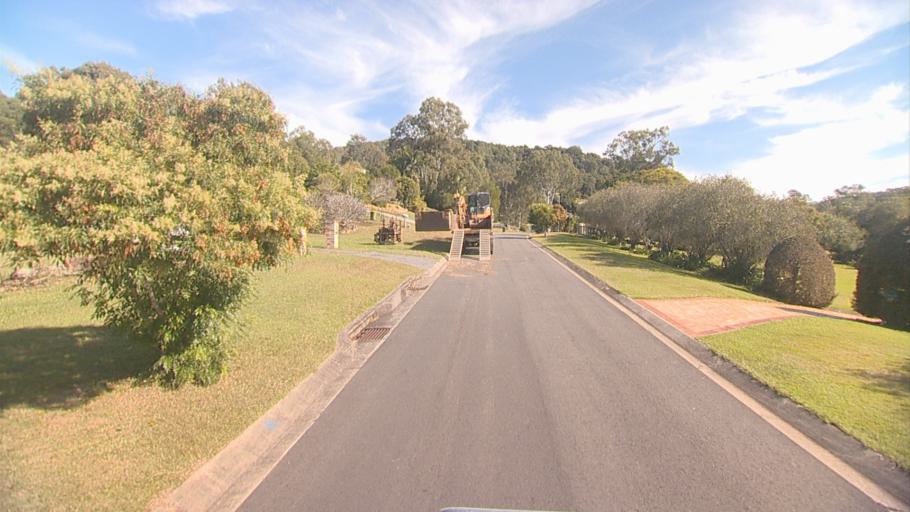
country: AU
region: Queensland
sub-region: Logan
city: Windaroo
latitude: -27.7571
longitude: 153.1754
